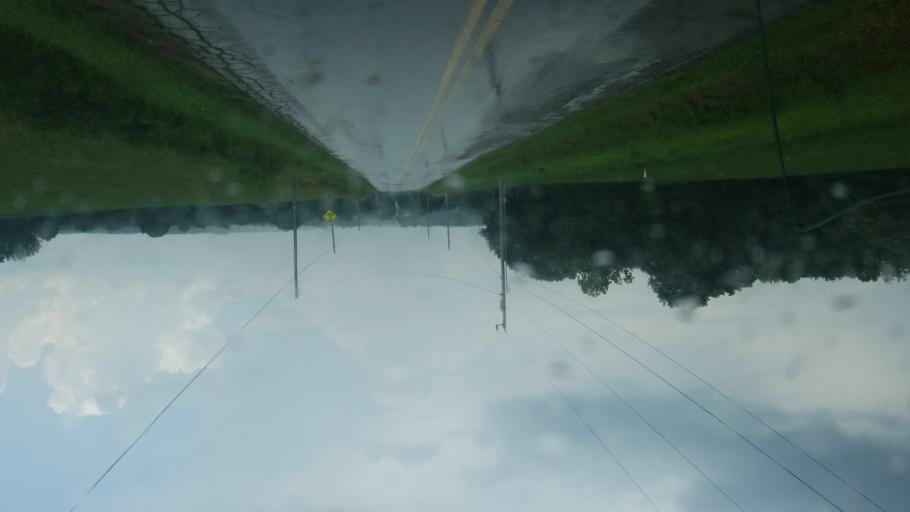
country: US
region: Ohio
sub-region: Wayne County
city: Smithville
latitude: 40.9018
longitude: -81.8323
